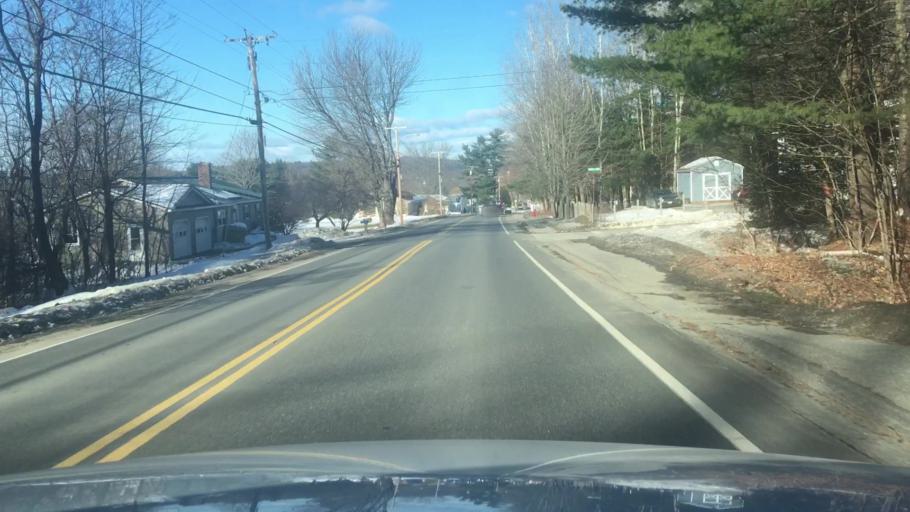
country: US
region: Maine
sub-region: Somerset County
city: Skowhegan
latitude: 44.7531
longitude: -69.7087
